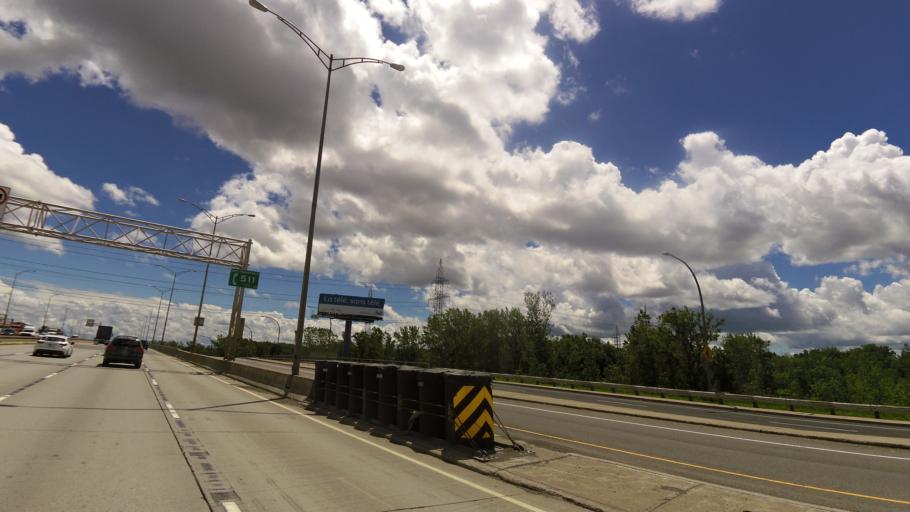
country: CA
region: Quebec
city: Dorval
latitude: 45.5061
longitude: -73.7594
